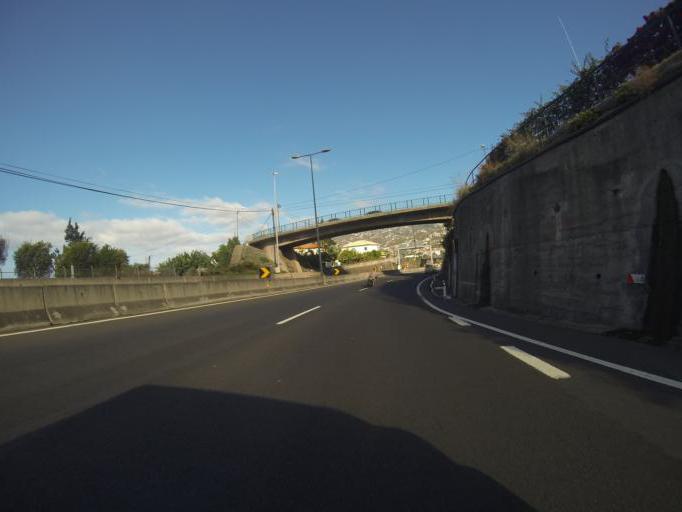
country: PT
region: Madeira
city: Camara de Lobos
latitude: 32.6503
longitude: -16.9594
